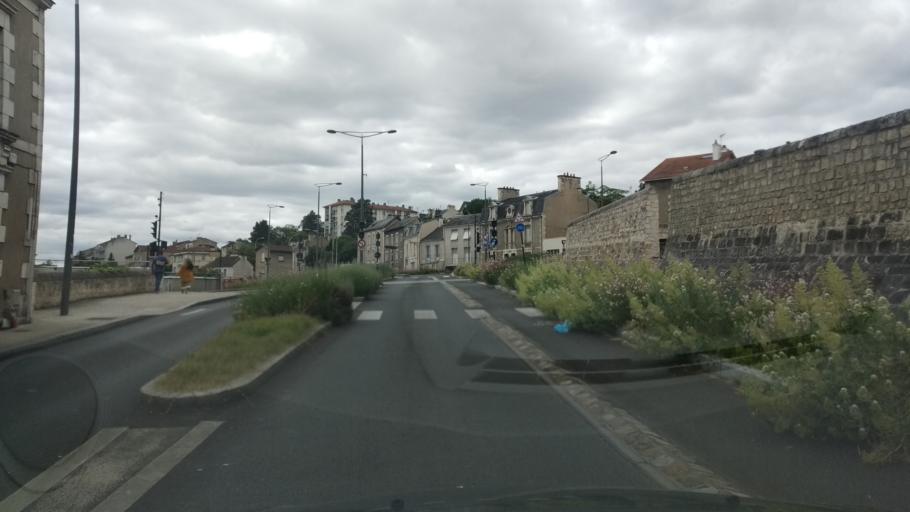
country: FR
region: Poitou-Charentes
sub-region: Departement de la Vienne
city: Poitiers
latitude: 46.5859
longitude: 0.3336
